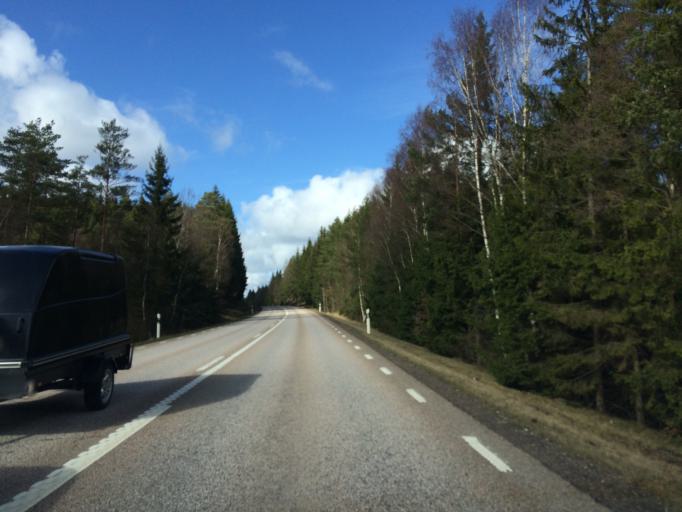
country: SE
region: Kronoberg
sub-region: Markaryds Kommun
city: Markaryd
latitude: 56.4844
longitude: 13.4803
